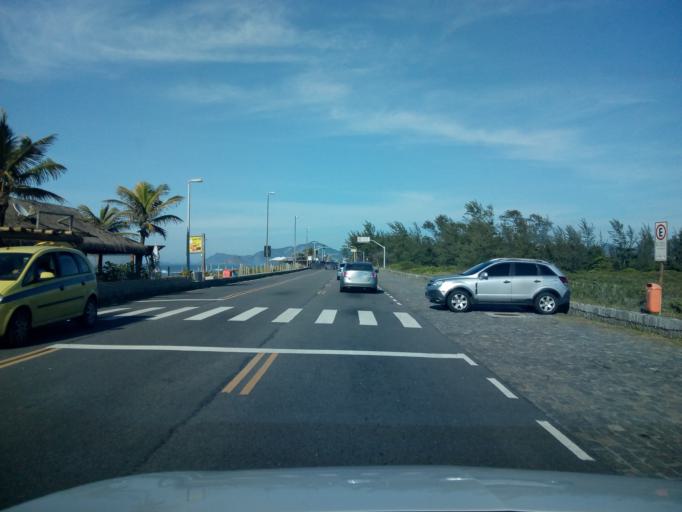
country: BR
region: Rio de Janeiro
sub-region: Nilopolis
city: Nilopolis
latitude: -23.0135
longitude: -43.3977
